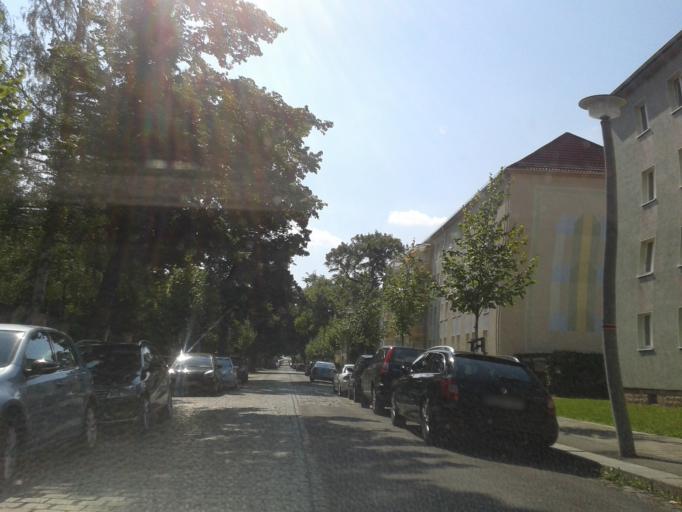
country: DE
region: Saxony
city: Dresden
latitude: 51.0374
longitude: 13.7288
